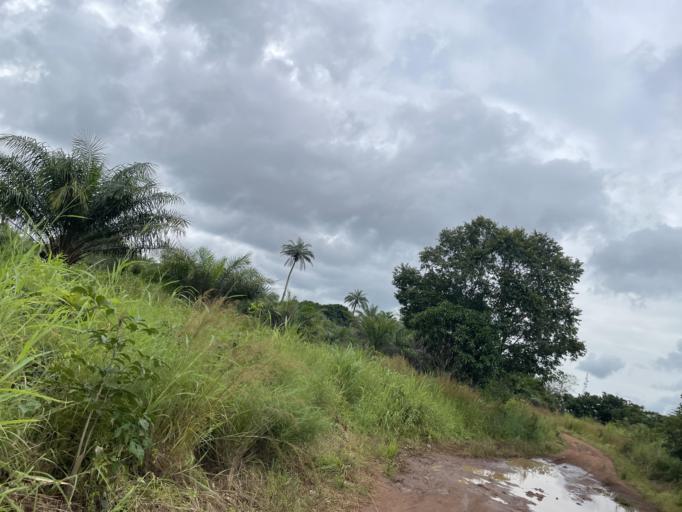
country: SL
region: Northern Province
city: Kambia
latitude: 9.1264
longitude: -12.8987
